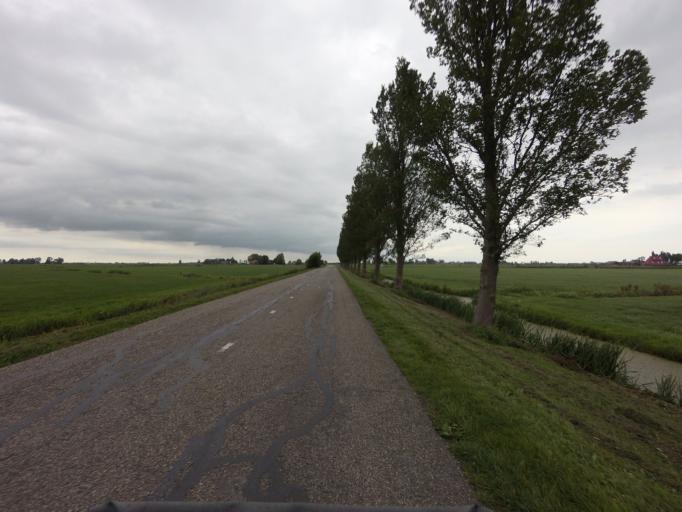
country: NL
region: Friesland
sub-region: Sudwest Fryslan
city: IJlst
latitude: 53.0192
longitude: 5.5987
